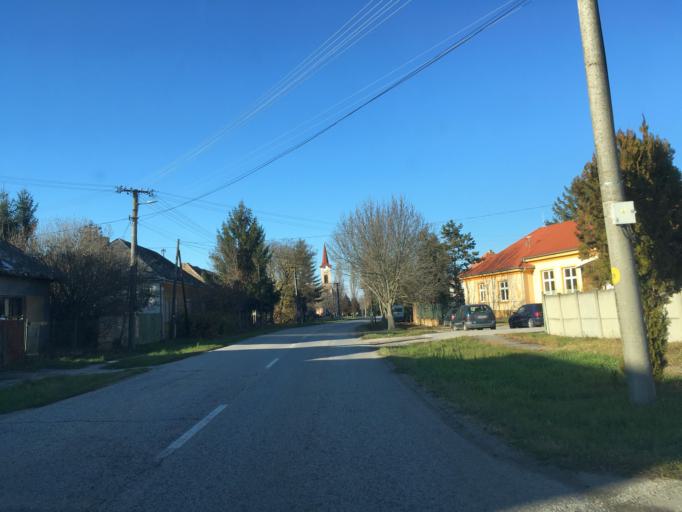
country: SK
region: Nitriansky
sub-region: Okres Komarno
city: Hurbanovo
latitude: 47.9030
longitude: 18.1373
